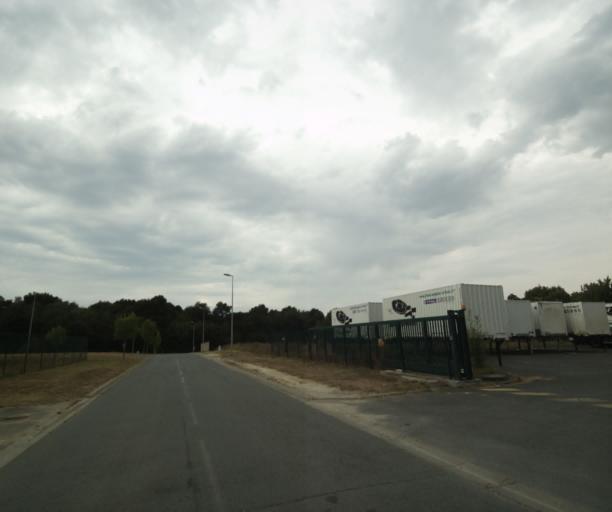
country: FR
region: Poitou-Charentes
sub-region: Departement de la Charente-Maritime
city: Tonnay-Charente
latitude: 45.9528
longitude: -0.8982
